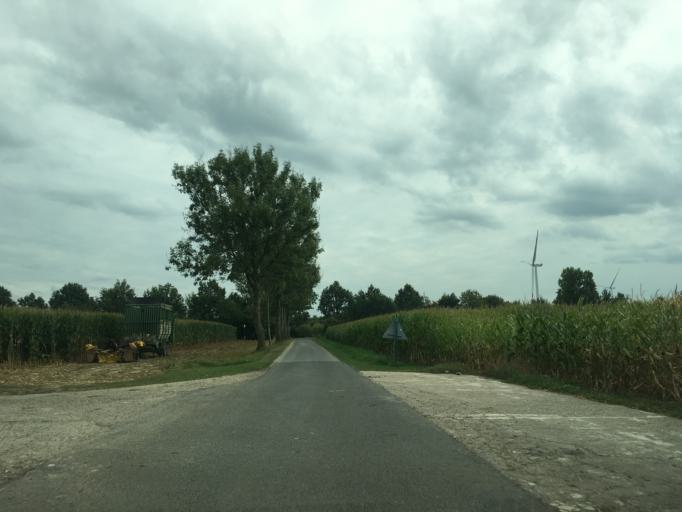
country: DE
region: North Rhine-Westphalia
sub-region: Regierungsbezirk Munster
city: Muenster
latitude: 51.9788
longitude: 7.5400
